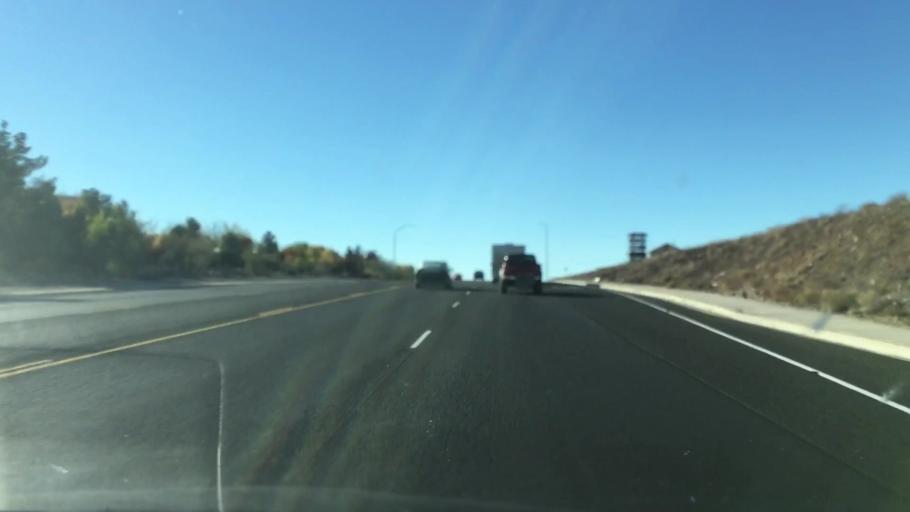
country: US
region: Utah
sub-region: Washington County
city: Hurricane
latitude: 37.1762
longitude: -113.3235
